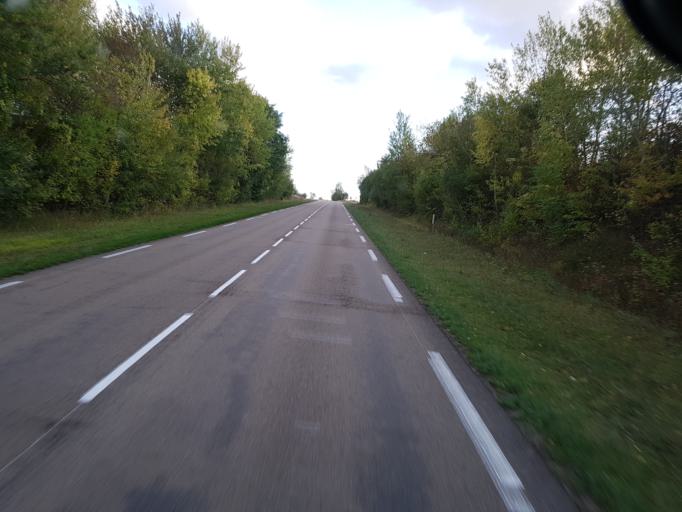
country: FR
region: Bourgogne
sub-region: Departement de l'Yonne
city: Soucy
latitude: 48.2772
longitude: 3.2719
